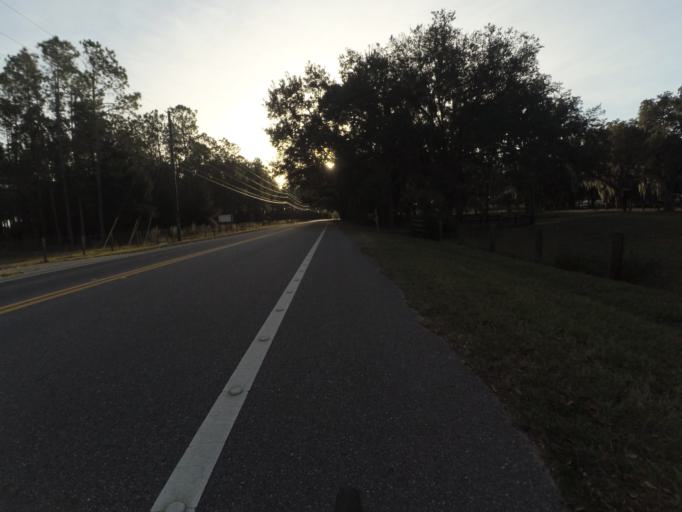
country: US
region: Florida
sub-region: Lake County
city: Umatilla
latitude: 28.9357
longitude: -81.7029
